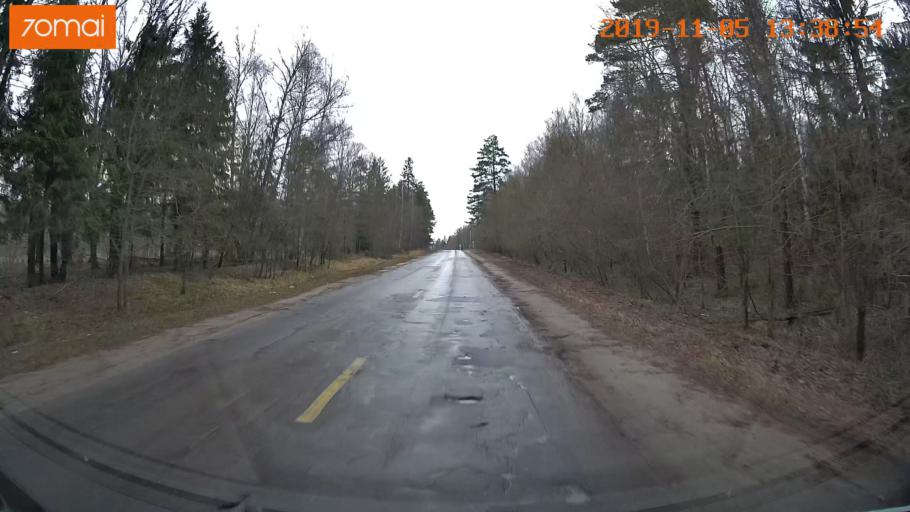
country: RU
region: Ivanovo
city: Shuya
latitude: 56.9354
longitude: 41.3869
